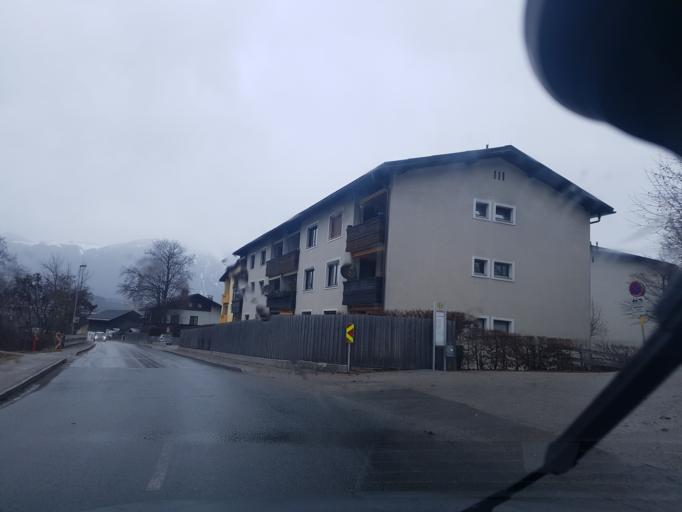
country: AT
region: Tyrol
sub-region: Politischer Bezirk Kufstein
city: Worgl
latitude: 47.4803
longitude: 12.0718
